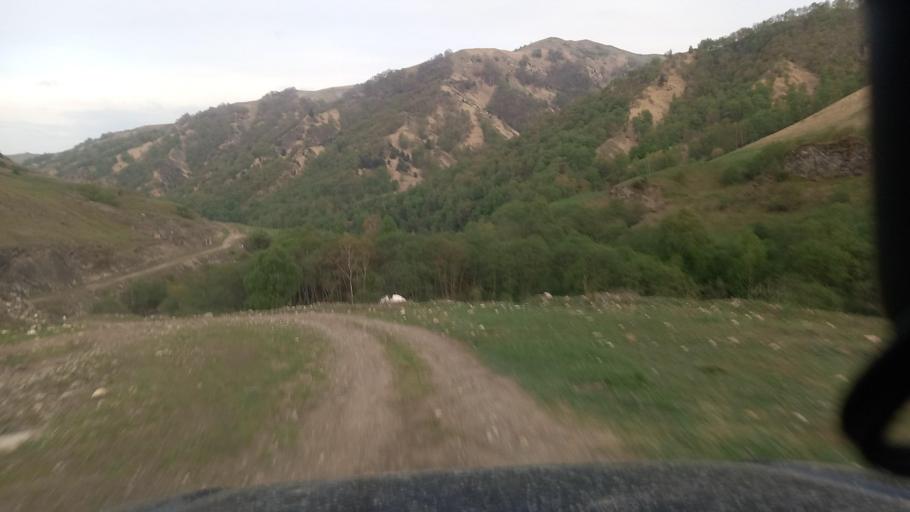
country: RU
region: Kabardino-Balkariya
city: Kamennomostskoye
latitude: 43.7197
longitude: 42.8739
